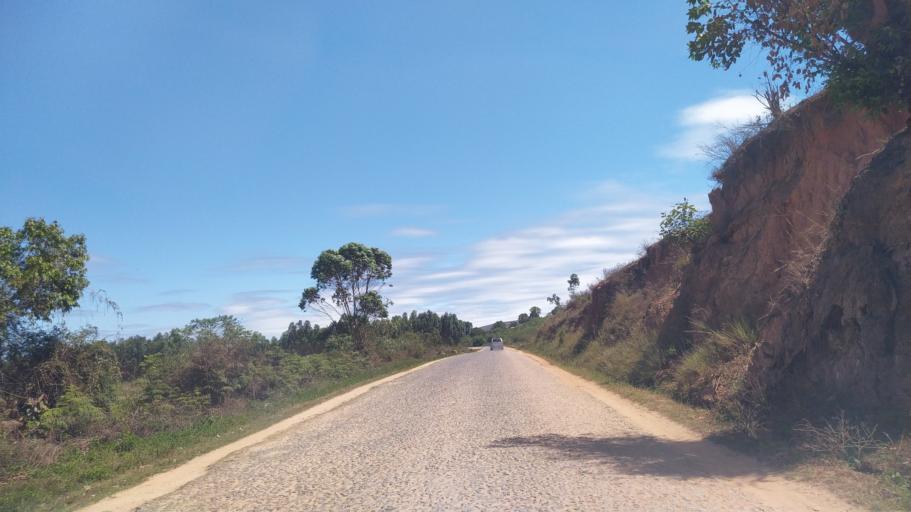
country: MG
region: Alaotra Mangoro
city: Moramanga
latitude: -18.7362
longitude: 48.2656
